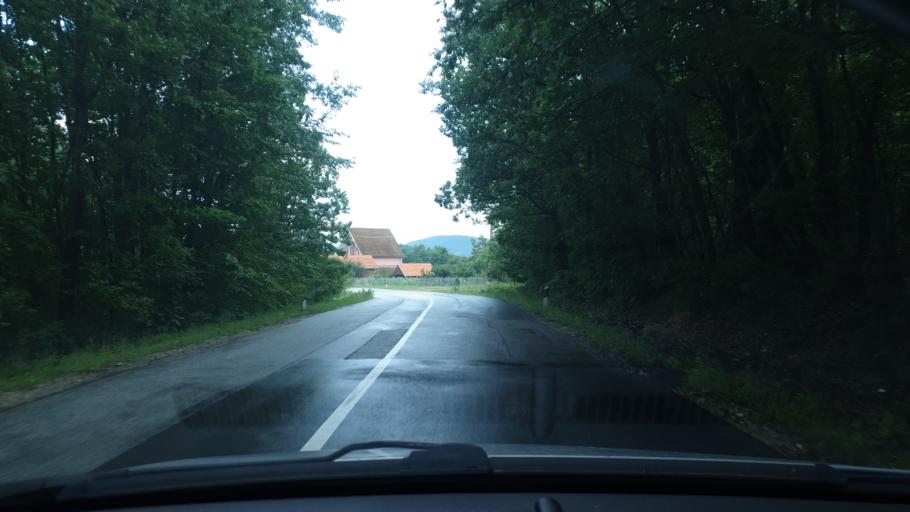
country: RS
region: Central Serbia
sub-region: Sumadijski Okrug
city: Kragujevac
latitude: 44.0469
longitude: 20.7866
